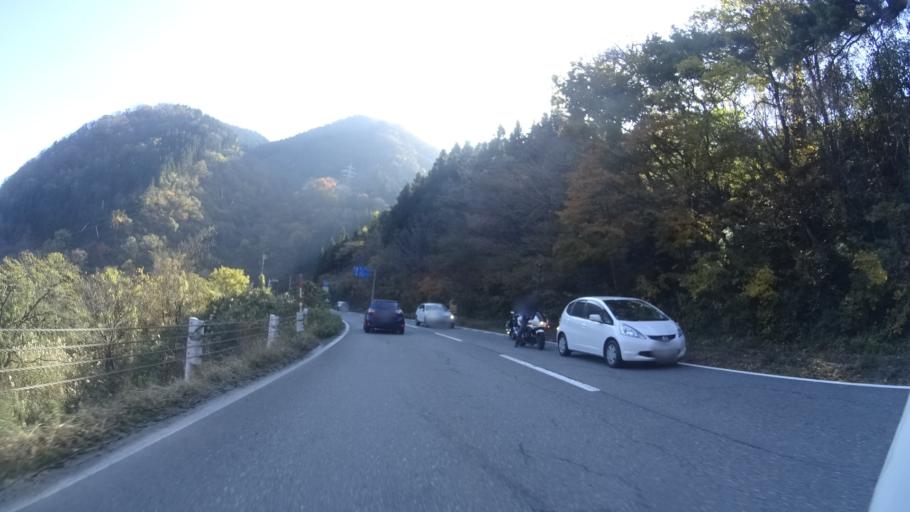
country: JP
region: Fukui
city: Ono
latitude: 35.9635
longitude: 136.6056
